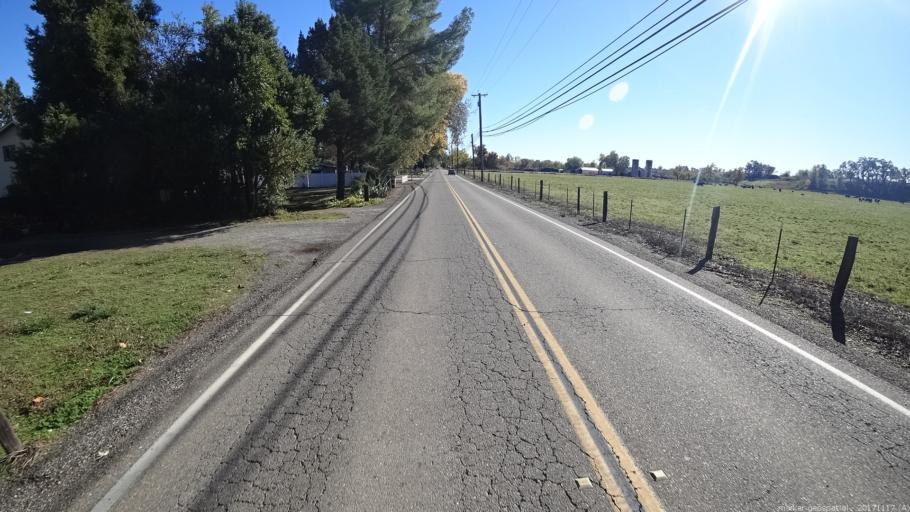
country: US
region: California
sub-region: Shasta County
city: Anderson
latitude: 40.4468
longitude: -122.2546
